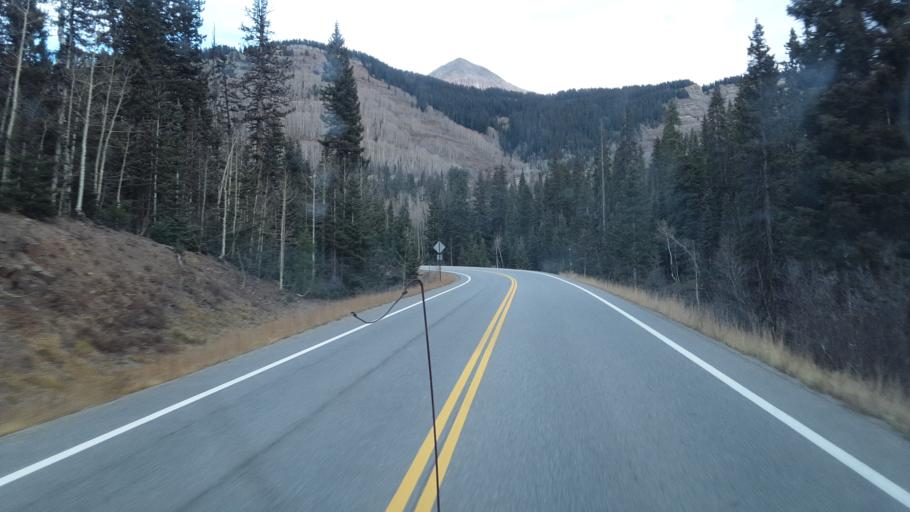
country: US
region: Colorado
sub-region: San Juan County
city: Silverton
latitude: 37.6751
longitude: -107.7905
